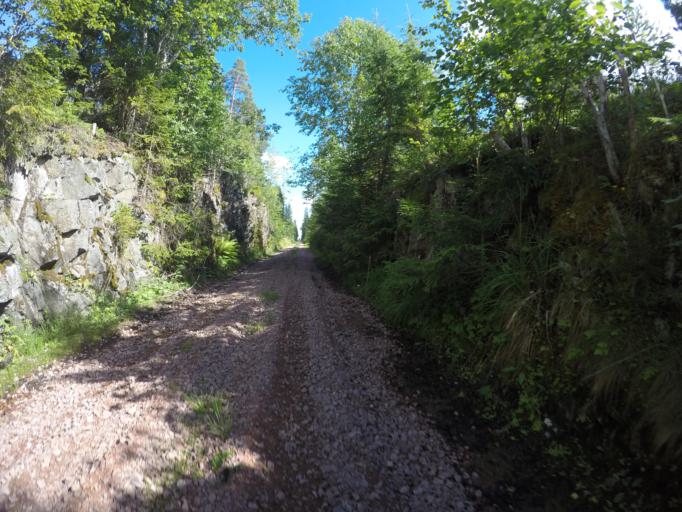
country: SE
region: OErebro
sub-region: Hallefors Kommun
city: Haellefors
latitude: 60.0242
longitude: 14.5728
